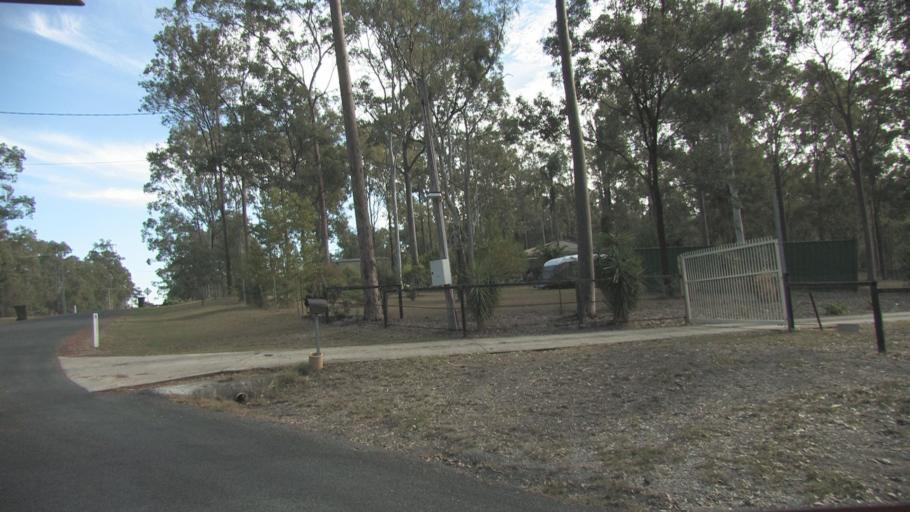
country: AU
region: Queensland
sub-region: Logan
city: North Maclean
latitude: -27.7787
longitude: 152.9744
